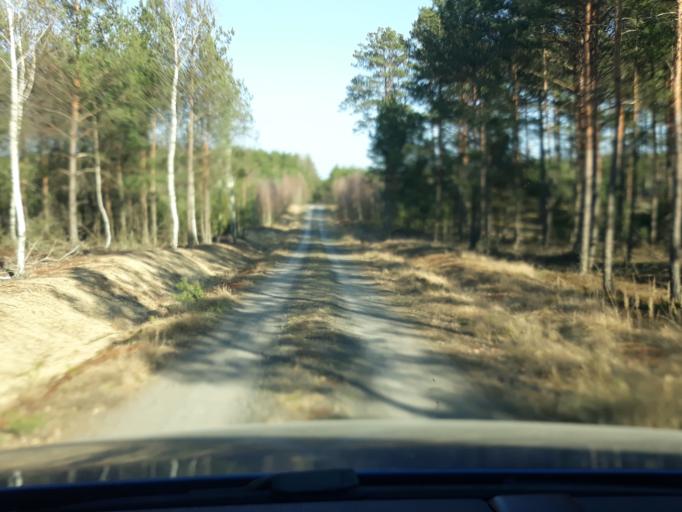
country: PL
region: Pomeranian Voivodeship
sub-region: Powiat bytowski
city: Lipnica
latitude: 53.9137
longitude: 17.4864
